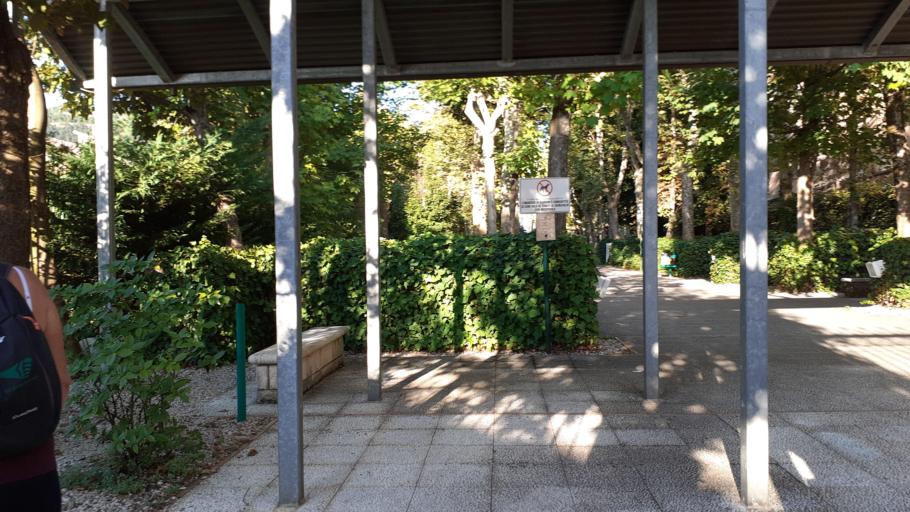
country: IT
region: Abruzzo
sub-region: Provincia di Pescara
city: Caramanico Terme
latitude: 42.1592
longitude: 14.0047
